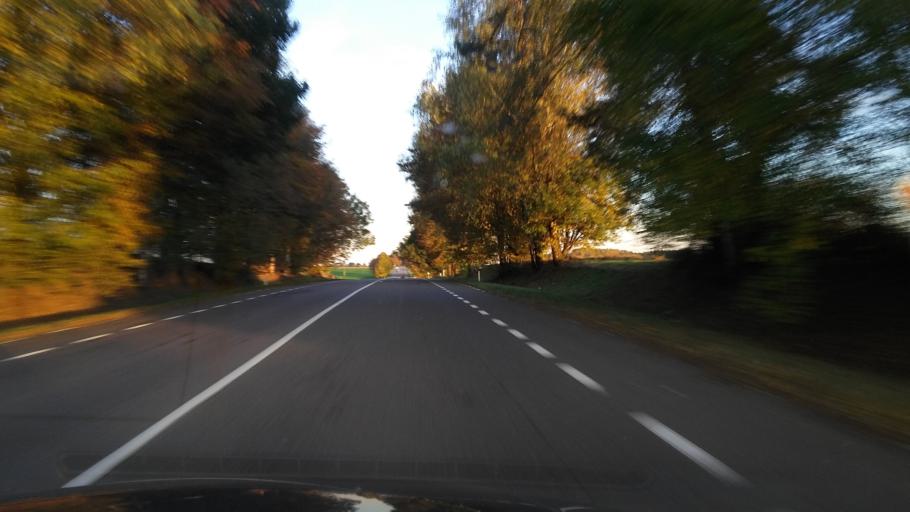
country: BE
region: Wallonia
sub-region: Province du Luxembourg
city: Florenville
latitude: 49.6999
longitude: 5.2664
